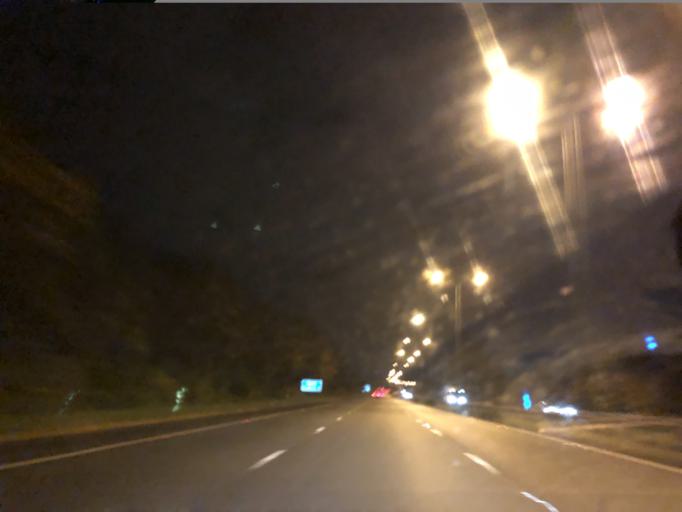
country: GB
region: England
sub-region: Kirklees
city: Cleckheaton
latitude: 53.7443
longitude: -1.7337
